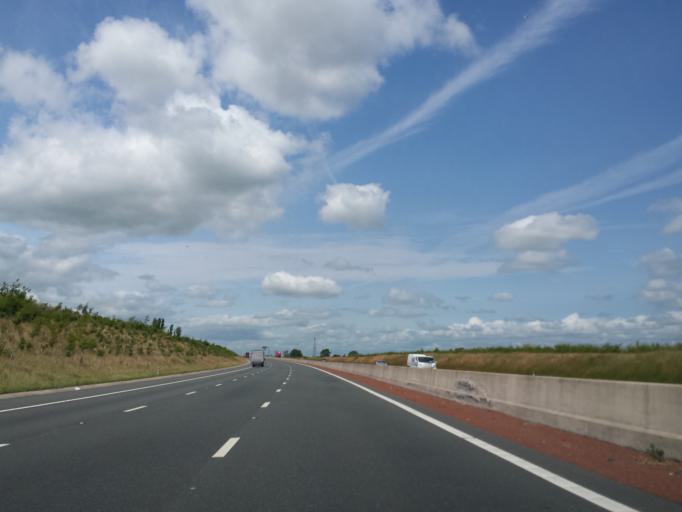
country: GB
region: England
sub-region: North Yorkshire
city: Ripon
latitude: 54.2173
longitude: -1.4817
